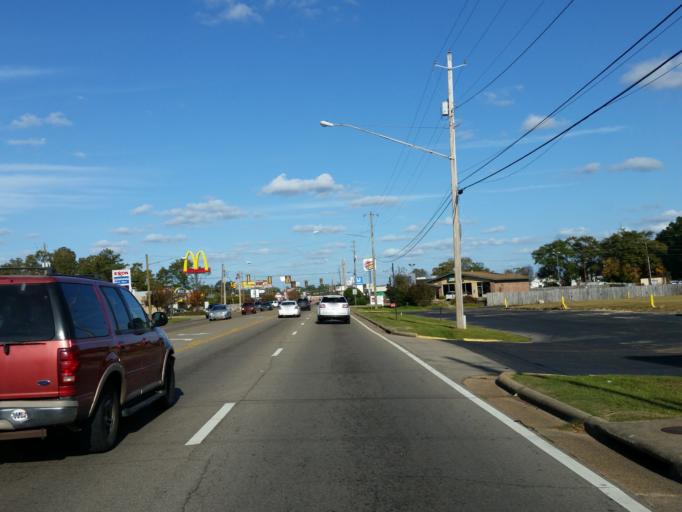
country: US
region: Mississippi
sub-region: Forrest County
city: Hattiesburg
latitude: 31.3103
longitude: -89.3131
